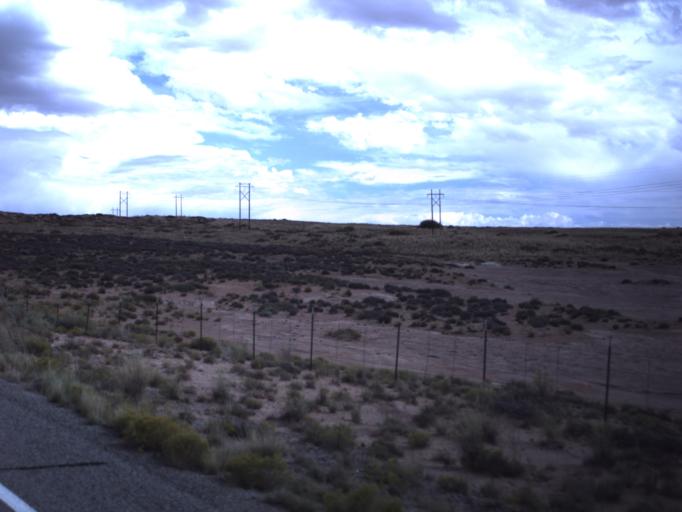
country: US
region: Utah
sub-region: San Juan County
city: Blanding
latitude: 37.3010
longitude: -109.4503
